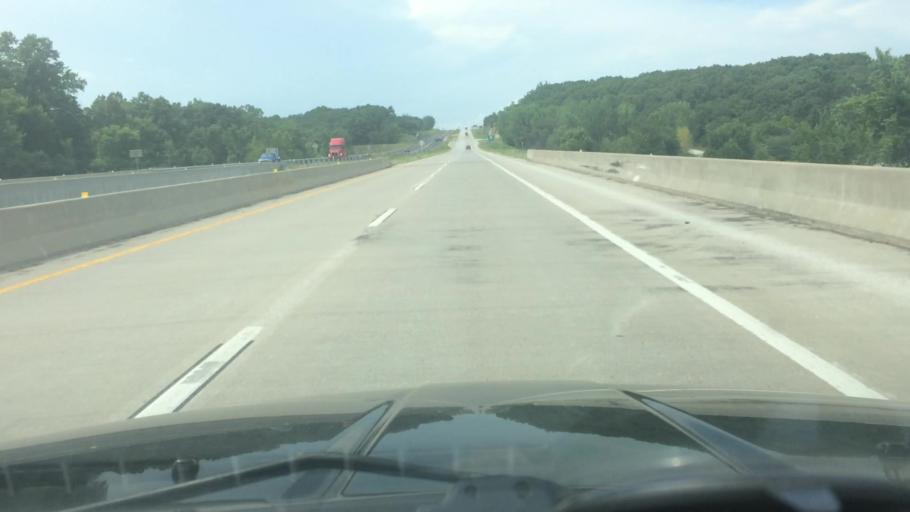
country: US
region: Missouri
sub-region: Saint Clair County
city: Osceola
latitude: 38.0617
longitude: -93.6936
